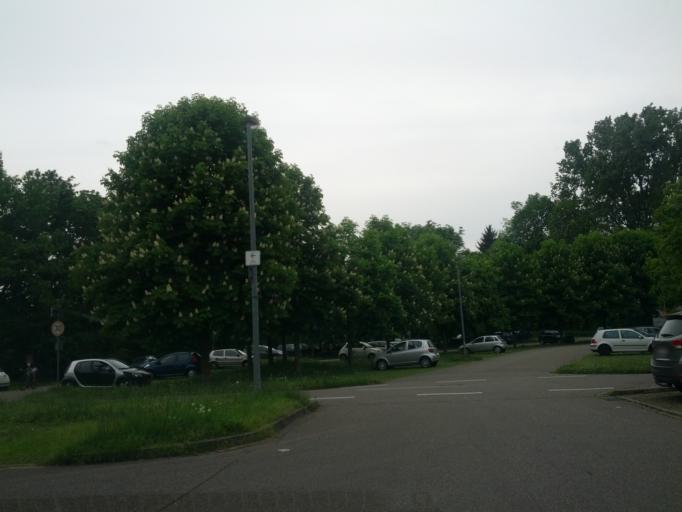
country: DE
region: Baden-Wuerttemberg
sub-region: Freiburg Region
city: Umkirch
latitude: 48.0124
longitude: 7.8062
